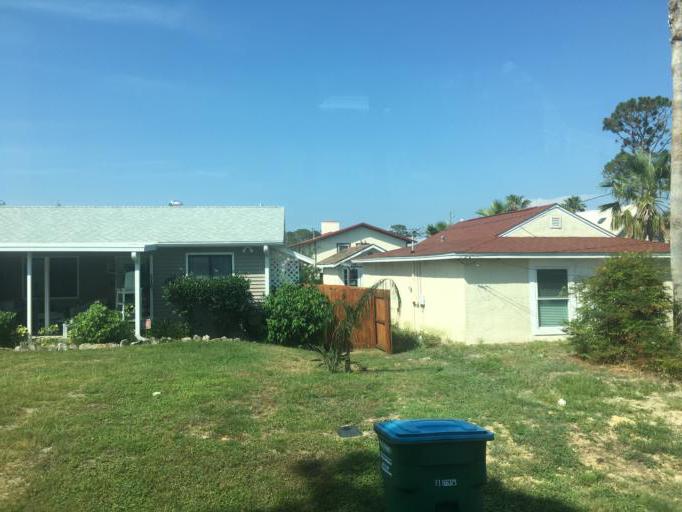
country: US
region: Florida
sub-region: Bay County
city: Panama City Beach
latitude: 30.1646
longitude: -85.7817
